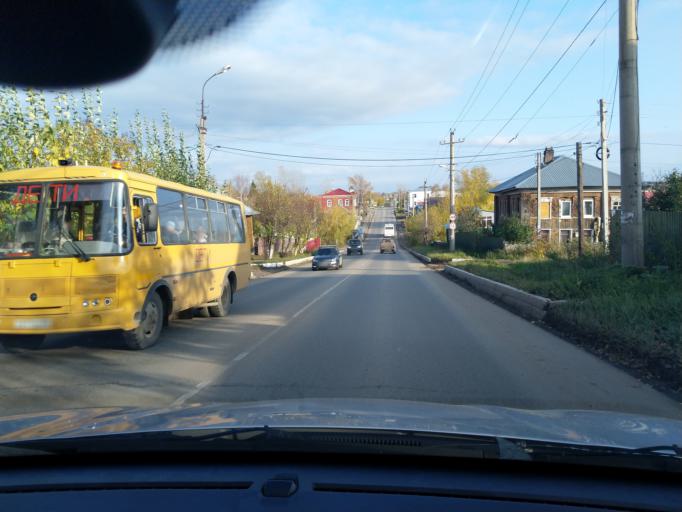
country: RU
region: Perm
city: Dobryanka
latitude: 58.4615
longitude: 56.4073
